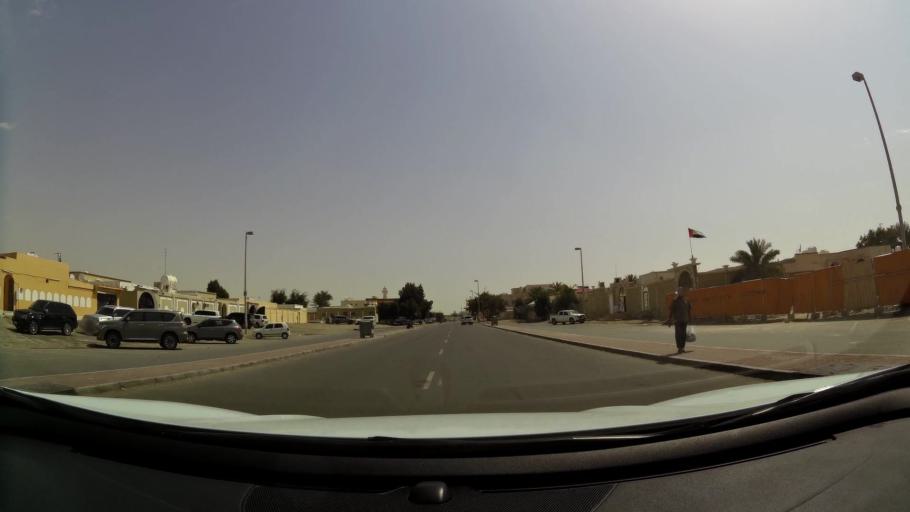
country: AE
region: Abu Dhabi
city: Abu Dhabi
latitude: 24.2909
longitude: 54.6531
